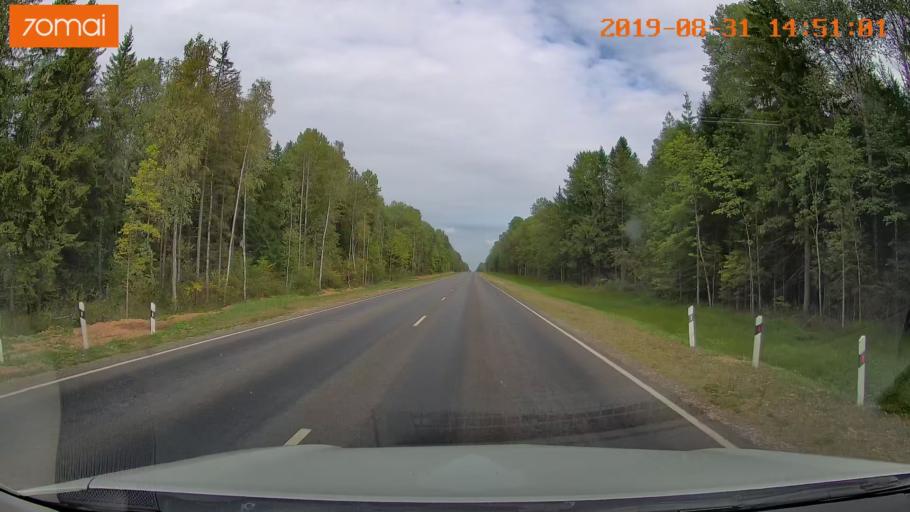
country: RU
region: Kaluga
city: Spas-Demensk
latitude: 54.2656
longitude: 33.8042
